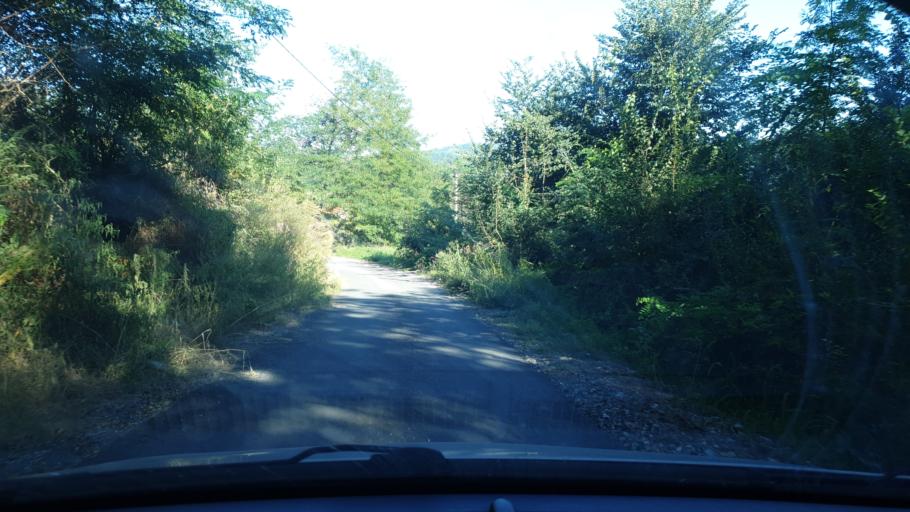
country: RS
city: Jarebice
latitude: 44.5032
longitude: 19.4862
